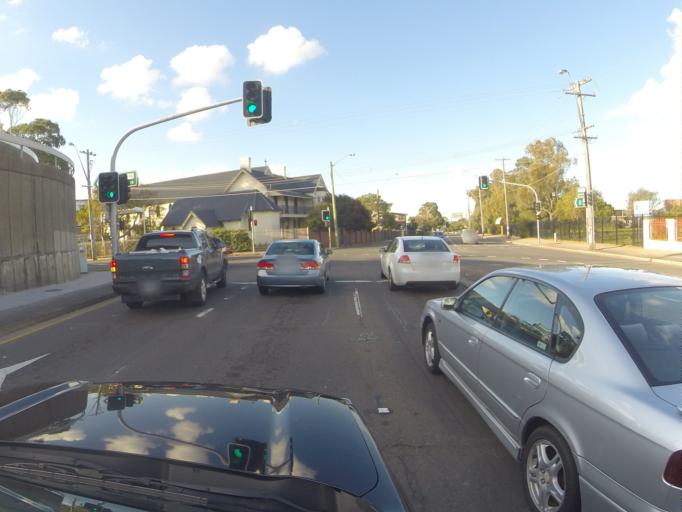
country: AU
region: New South Wales
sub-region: Rockdale
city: Bexley
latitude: -33.9624
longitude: 151.1125
